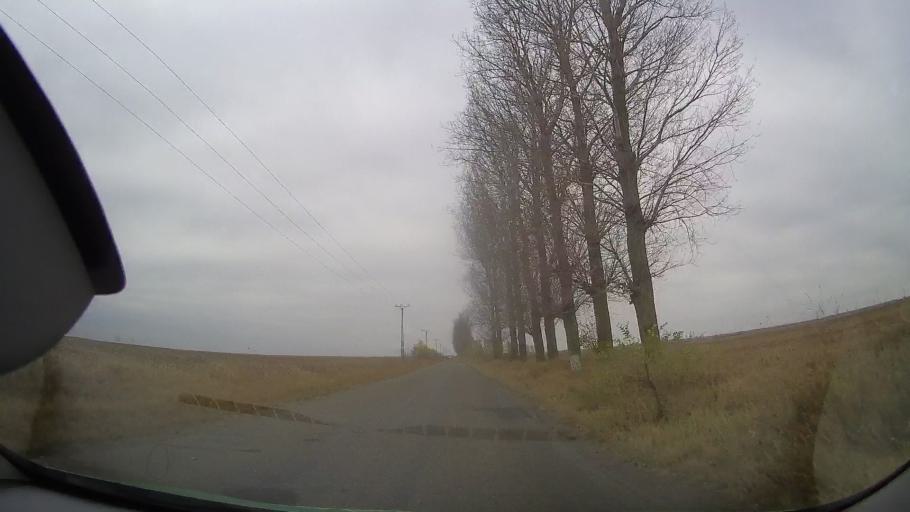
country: RO
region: Buzau
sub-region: Comuna Pogoanele
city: Pogoanele
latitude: 44.9585
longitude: 27.0195
